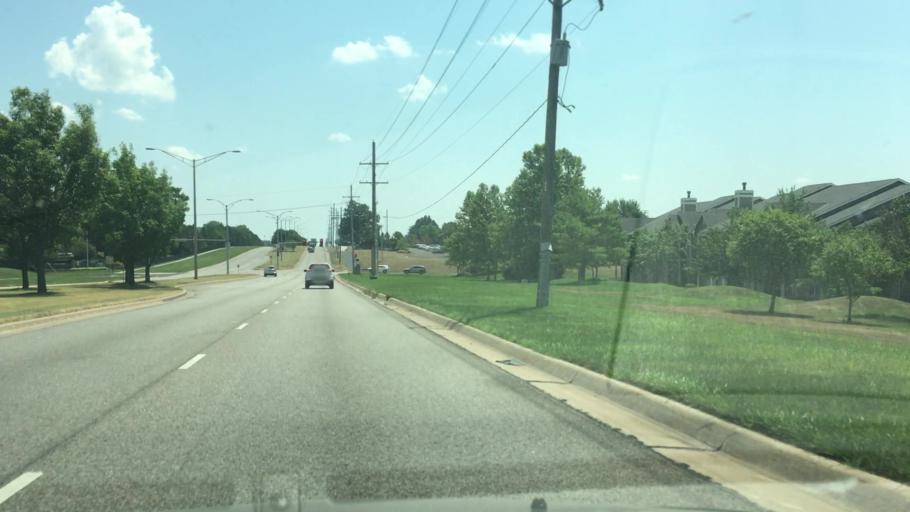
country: US
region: Kansas
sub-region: Johnson County
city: Lenexa
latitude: 38.8836
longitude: -94.7183
